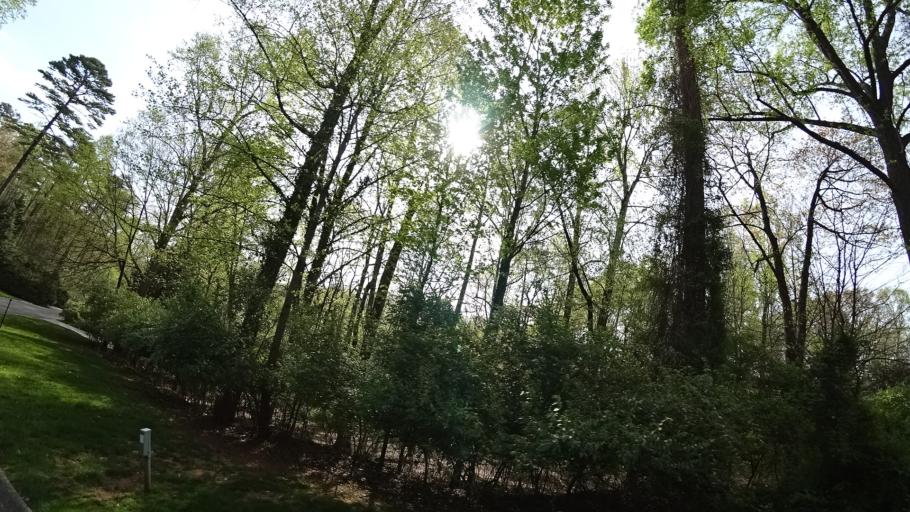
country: US
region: Tennessee
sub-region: Knox County
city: Knoxville
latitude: 35.9036
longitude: -83.9900
